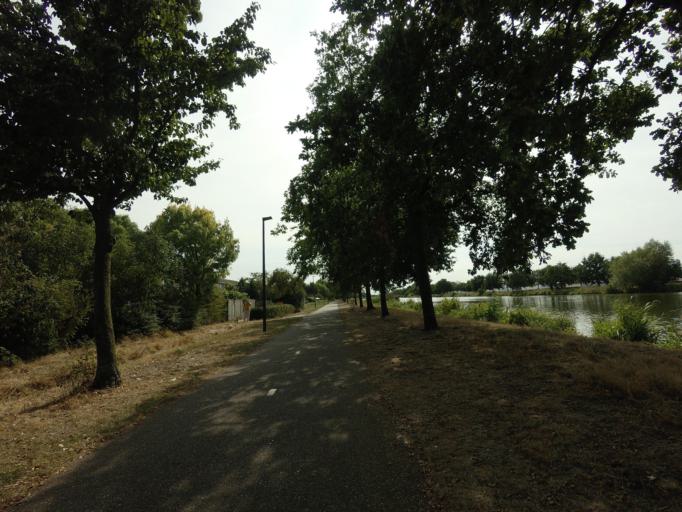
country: NL
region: North Brabant
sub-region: Gemeente Helmond
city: Helmond
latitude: 51.4621
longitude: 5.6954
